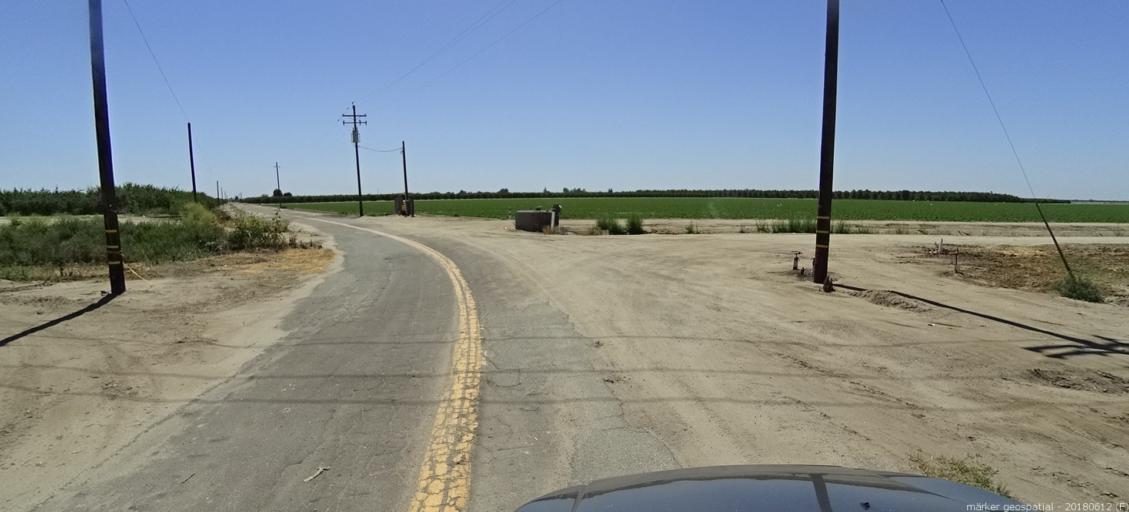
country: US
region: California
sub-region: Madera County
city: Chowchilla
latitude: 37.0254
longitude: -120.3416
